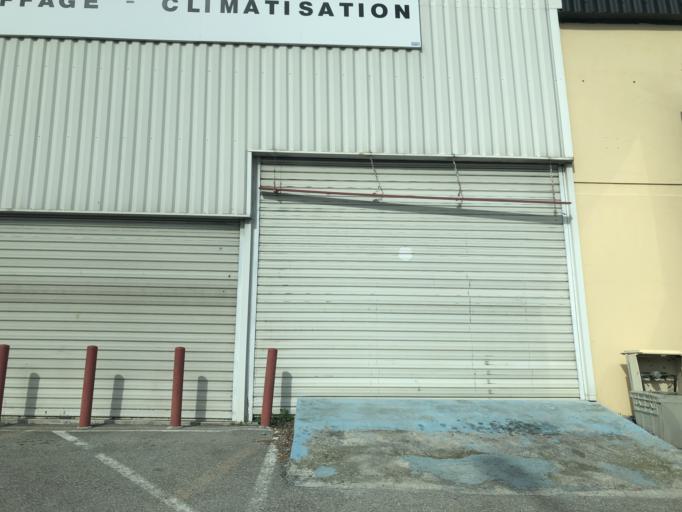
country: FR
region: Provence-Alpes-Cote d'Azur
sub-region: Departement des Alpes-Maritimes
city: Saint-Laurent-du-Var
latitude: 43.6964
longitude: 7.1845
